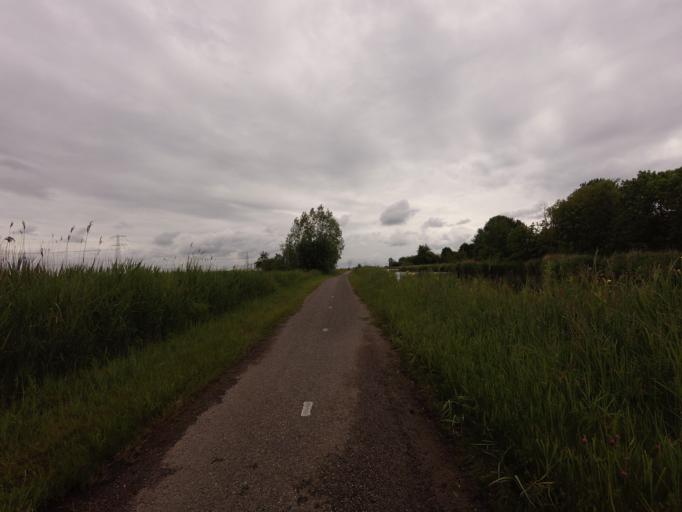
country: NL
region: North Holland
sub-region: Gemeente Waterland
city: Broek in Waterland
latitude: 52.3997
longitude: 4.9638
